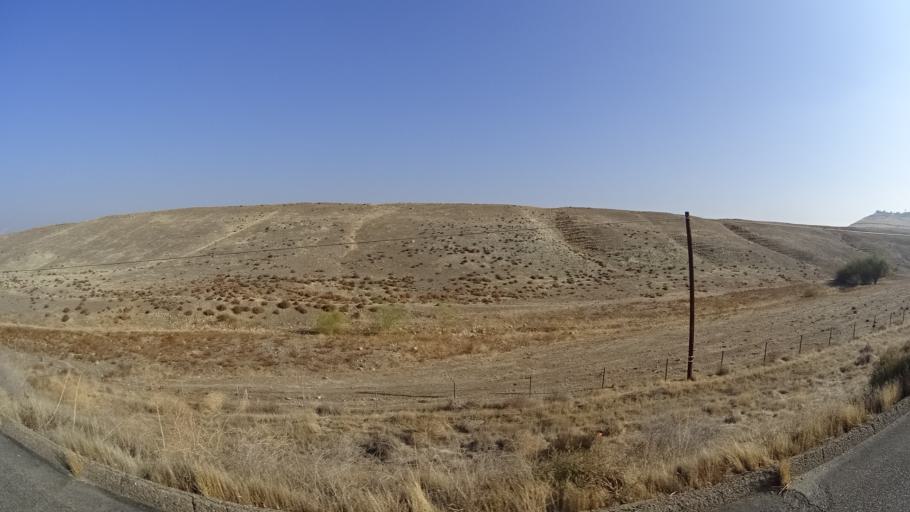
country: US
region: California
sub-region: Kern County
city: Oildale
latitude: 35.4242
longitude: -118.8588
